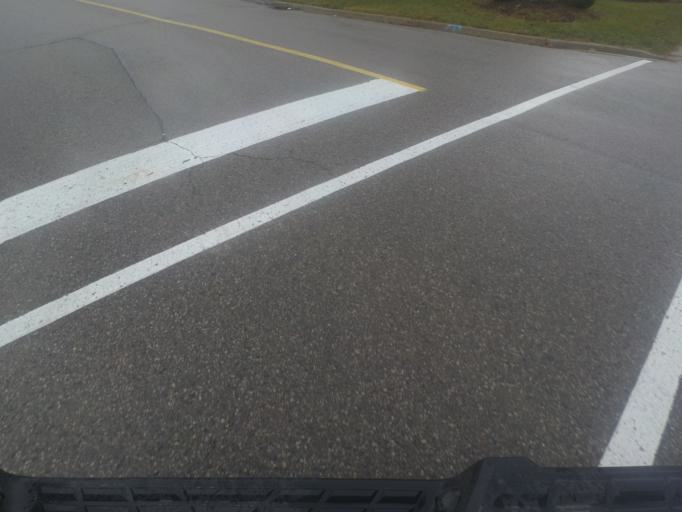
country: CN
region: Xinjiang Uygur Zizhiqu
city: Ayxin Siri
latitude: 43.4925
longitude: 80.5829
